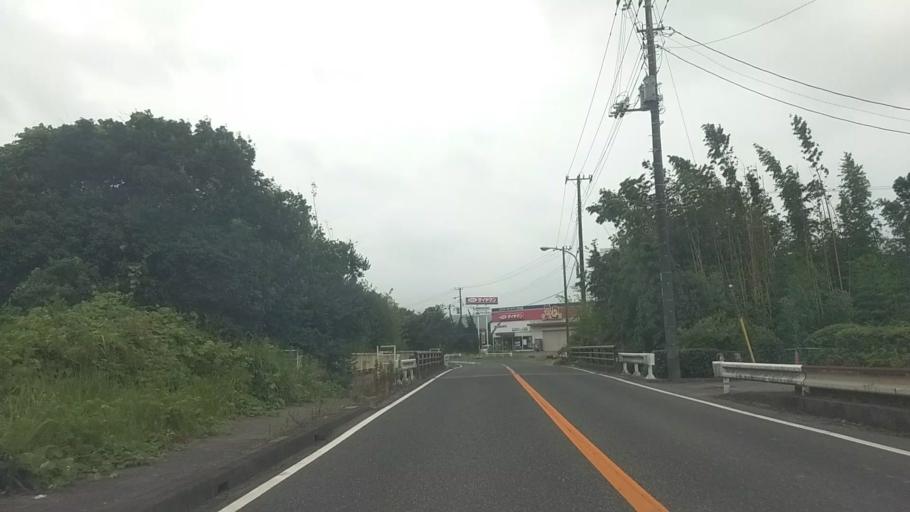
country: JP
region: Chiba
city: Kimitsu
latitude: 35.2177
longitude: 139.8911
